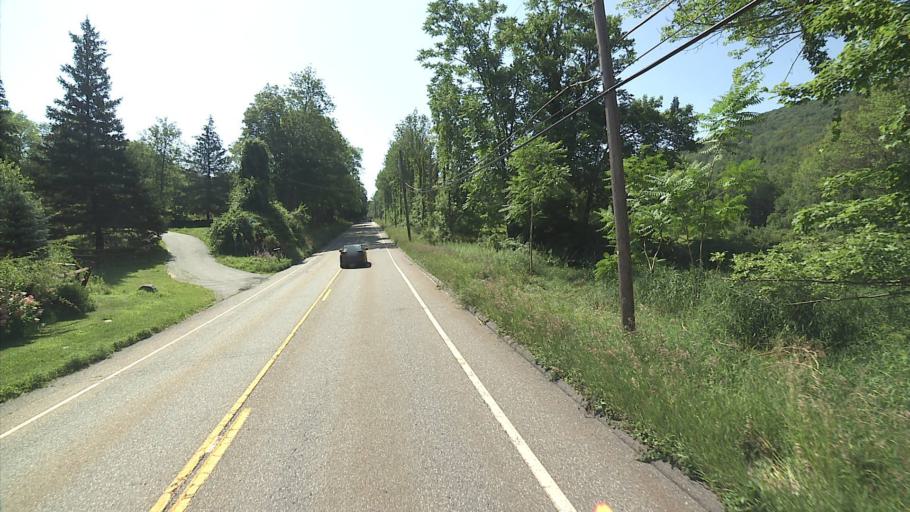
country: US
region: Connecticut
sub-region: Litchfield County
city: New Preston
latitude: 41.7953
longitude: -73.3685
